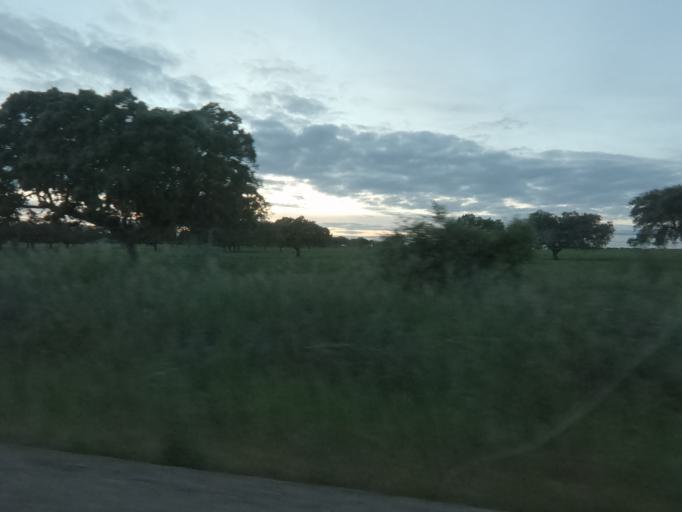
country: ES
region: Extremadura
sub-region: Provincia de Badajoz
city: Badajoz
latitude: 38.9592
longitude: -6.9040
